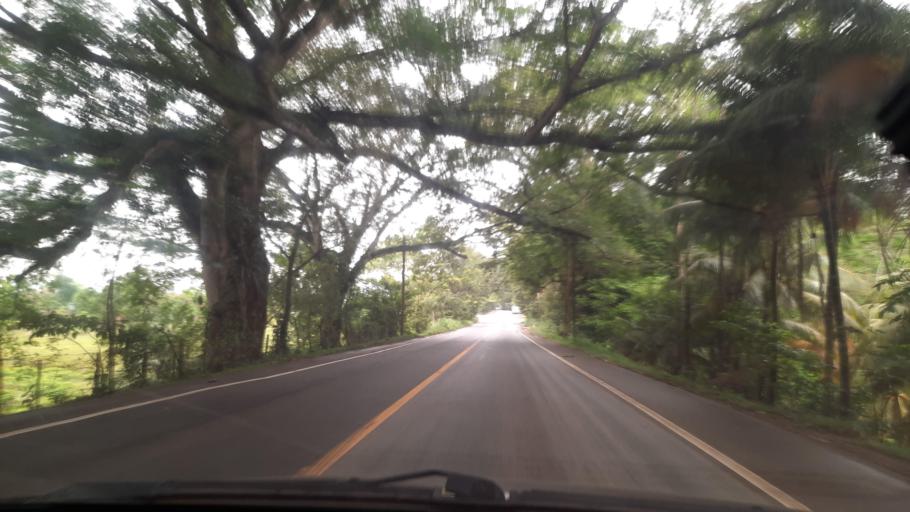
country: GT
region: Izabal
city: Morales
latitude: 15.4325
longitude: -88.9668
